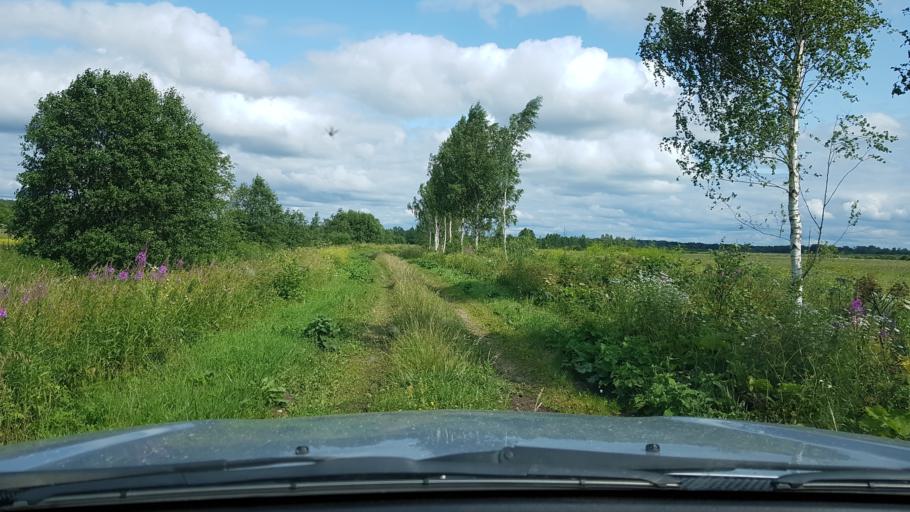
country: EE
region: Ida-Virumaa
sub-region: Narva-Joesuu linn
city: Narva-Joesuu
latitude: 59.3857
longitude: 27.9260
